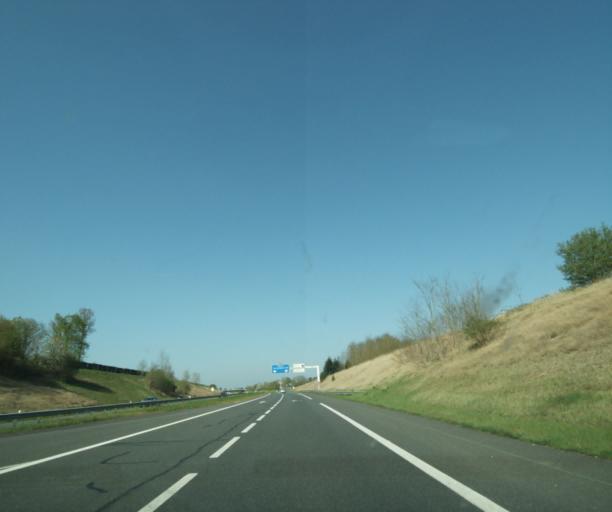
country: FR
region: Centre
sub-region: Departement du Loiret
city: Dordives
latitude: 48.1672
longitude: 2.7643
